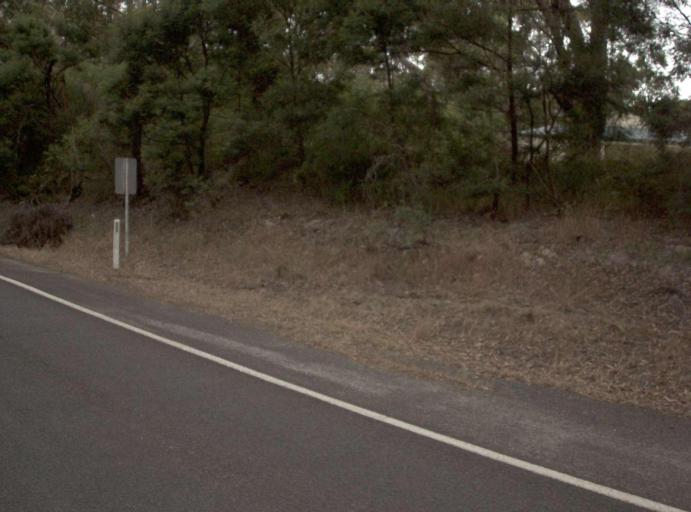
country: AU
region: Victoria
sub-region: Wellington
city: Sale
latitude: -38.5221
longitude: 146.8761
